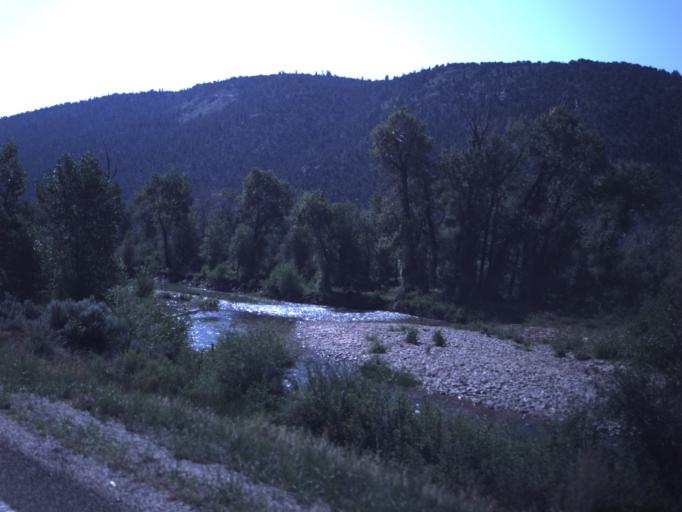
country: US
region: Utah
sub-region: Duchesne County
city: Duchesne
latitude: 40.3048
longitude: -110.6256
